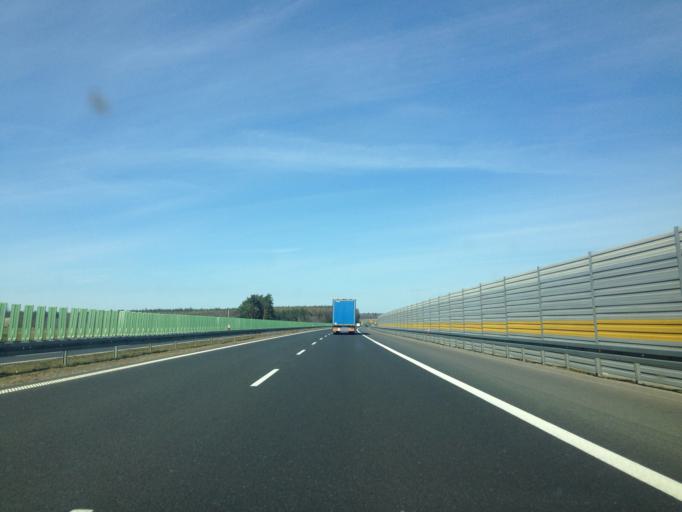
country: PL
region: Pomeranian Voivodeship
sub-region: Powiat starogardzki
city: Smetowo Graniczne
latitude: 53.8082
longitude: 18.6256
